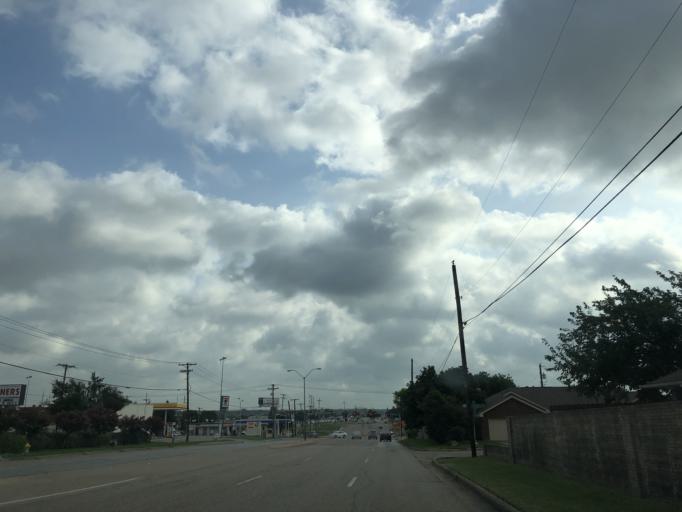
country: US
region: Texas
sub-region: Dallas County
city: Mesquite
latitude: 32.8328
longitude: -96.6351
